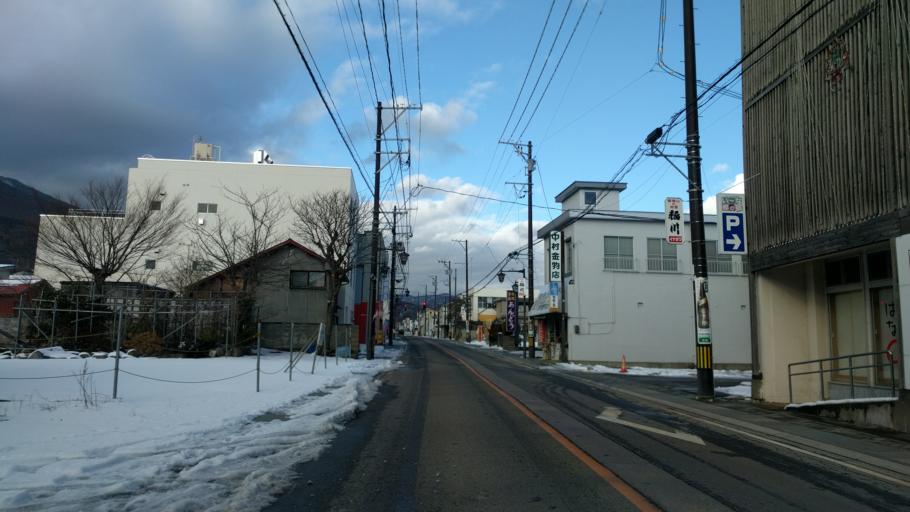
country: JP
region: Fukushima
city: Inawashiro
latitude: 37.5614
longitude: 140.1075
